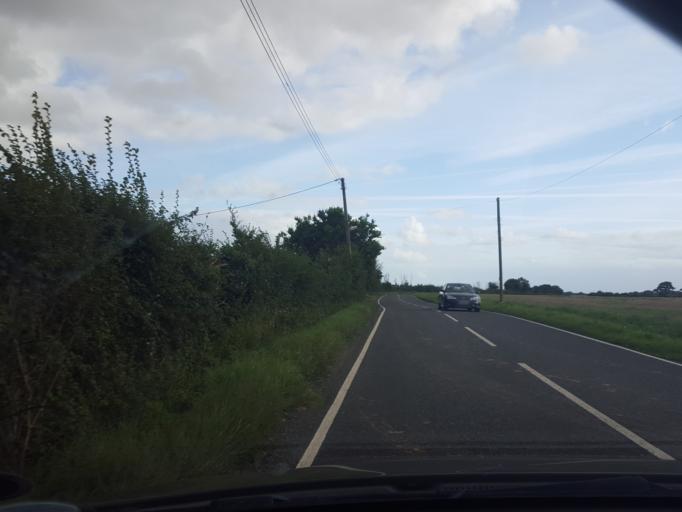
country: GB
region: England
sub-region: Essex
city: Little Clacton
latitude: 51.8383
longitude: 1.1546
